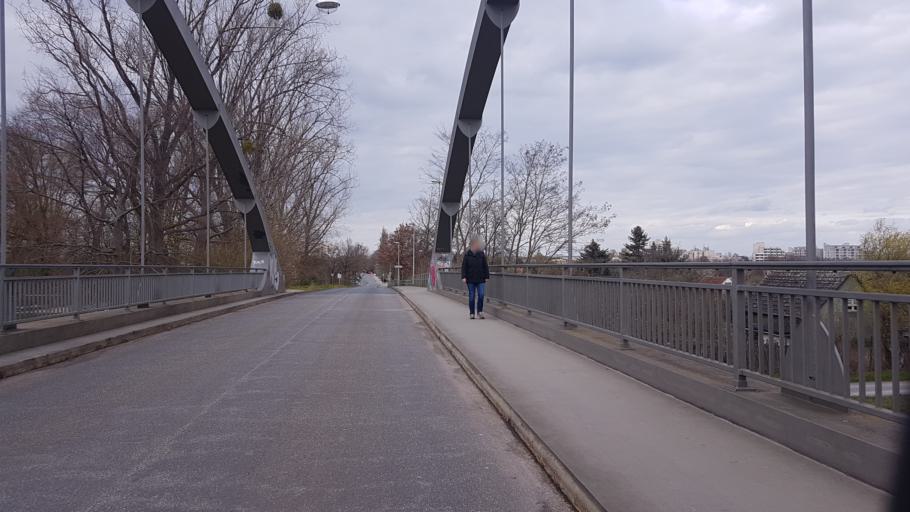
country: DE
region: Lower Saxony
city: Hannover
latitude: 52.4046
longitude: 9.7543
